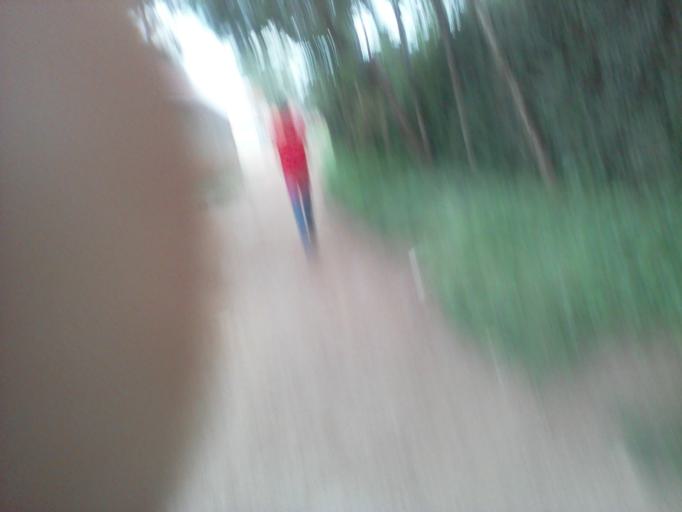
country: UG
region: Central Region
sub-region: Wakiso District
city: Wakiso
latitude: 0.4153
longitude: 32.5375
